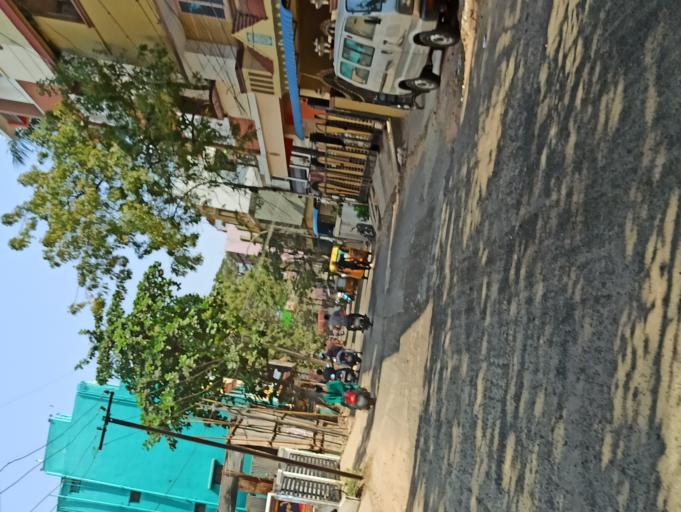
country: IN
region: Tamil Nadu
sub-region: Chennai
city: Chetput
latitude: 13.0609
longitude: 80.2263
